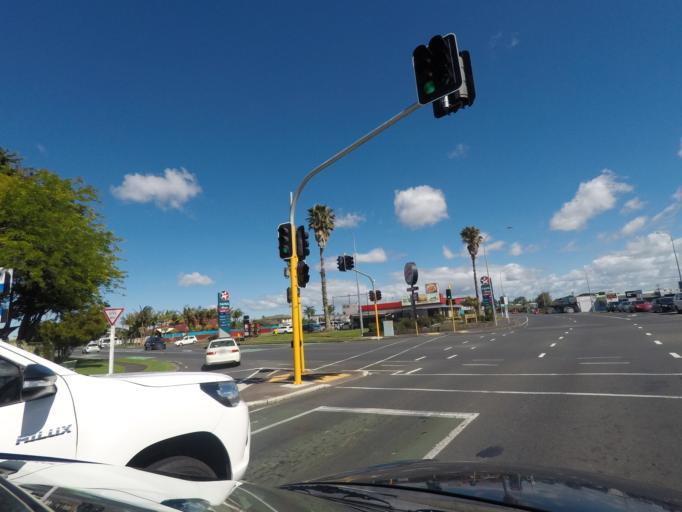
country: NZ
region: Auckland
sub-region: Auckland
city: Manukau City
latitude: -36.9817
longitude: 174.8776
